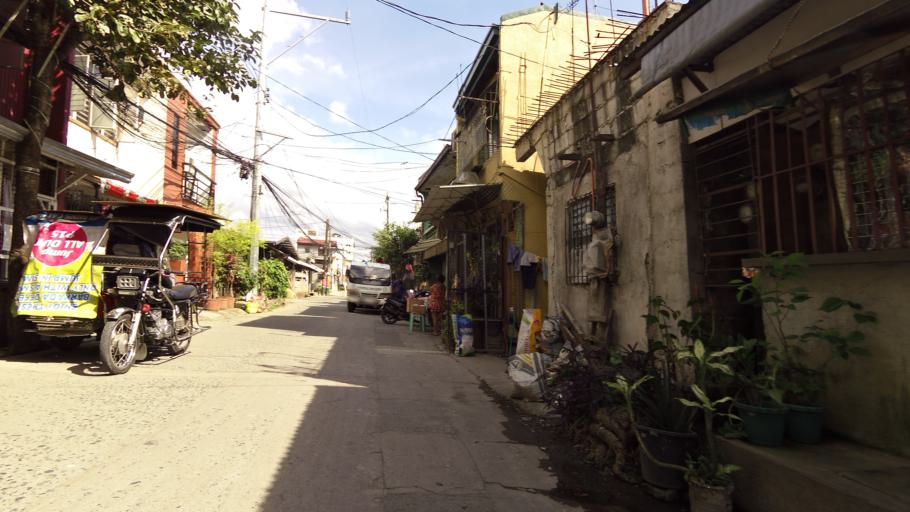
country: PH
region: Calabarzon
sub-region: Province of Rizal
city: Cainta
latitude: 14.5700
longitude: 121.1282
